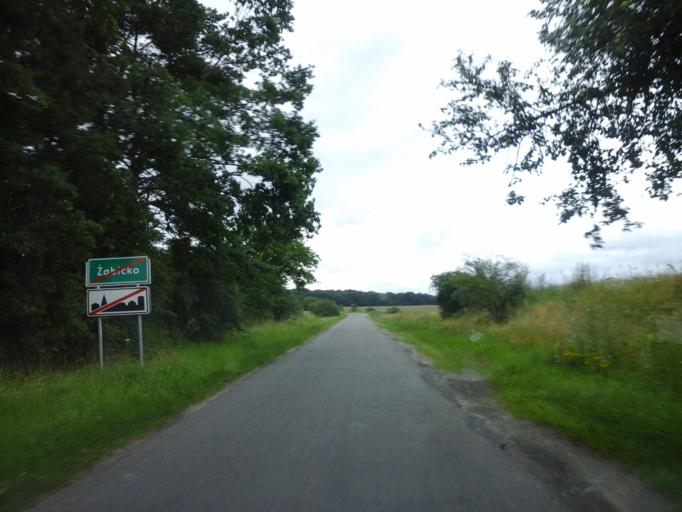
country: PL
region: West Pomeranian Voivodeship
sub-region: Powiat choszczenski
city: Krzecin
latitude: 52.9792
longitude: 15.4297
